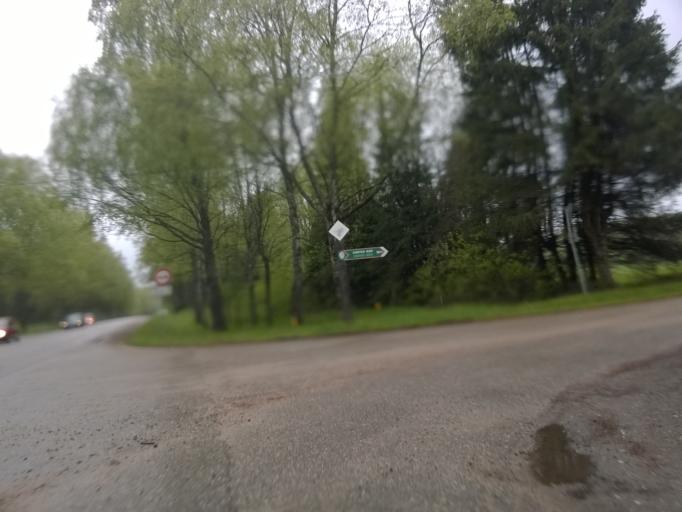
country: LV
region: Amatas Novads
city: Drabesi
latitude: 57.2175
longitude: 25.1981
